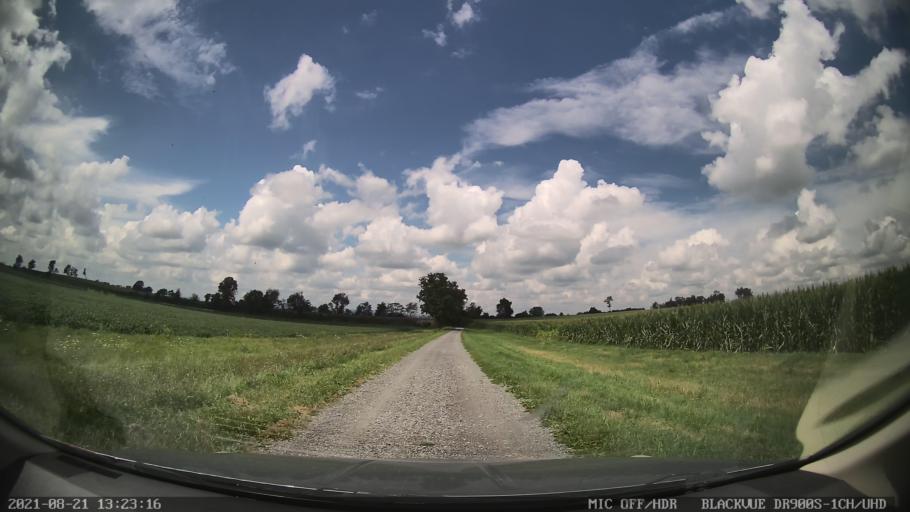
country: US
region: Pennsylvania
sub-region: Berks County
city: Fleetwood
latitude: 40.4697
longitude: -75.7801
